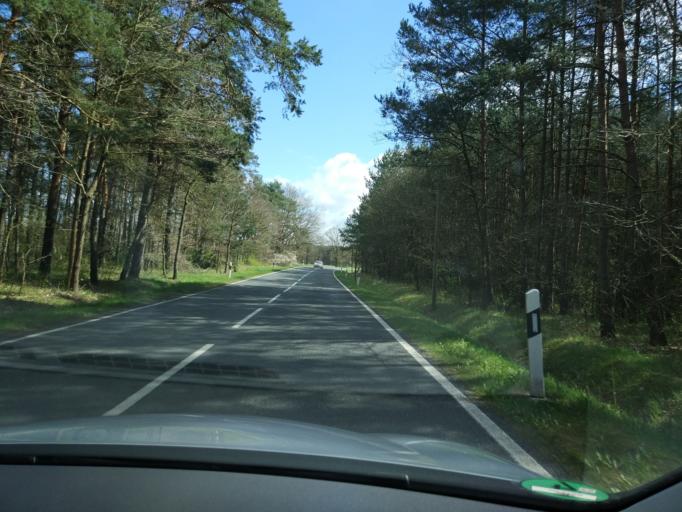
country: DE
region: Saxony-Anhalt
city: Oranienbaum
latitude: 51.7893
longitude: 12.4396
